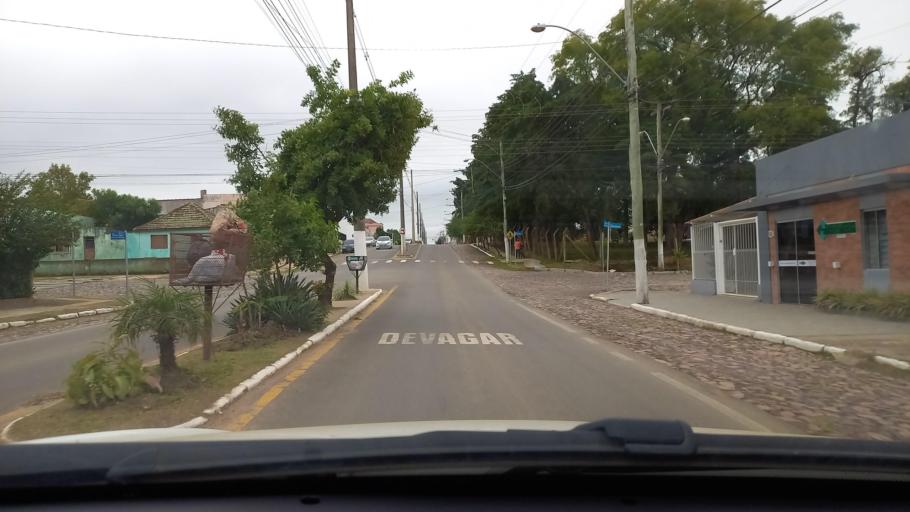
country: BR
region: Rio Grande do Sul
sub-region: Dom Pedrito
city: Dom Pedrito
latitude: -30.9841
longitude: -54.6670
